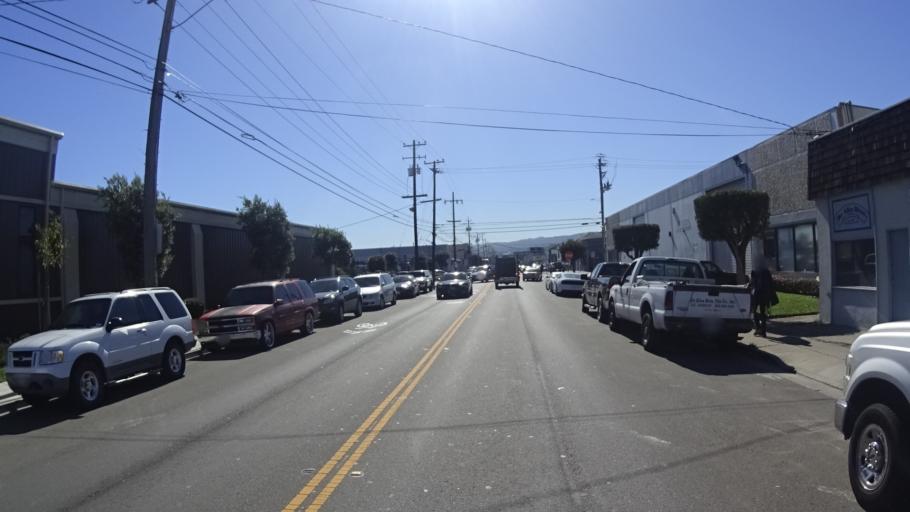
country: US
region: California
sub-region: San Mateo County
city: South San Francisco
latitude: 37.6474
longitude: -122.4128
